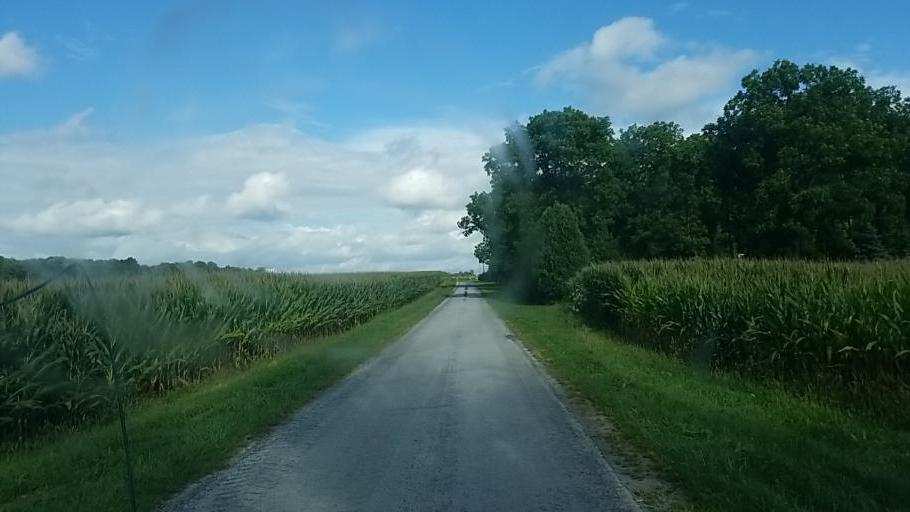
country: US
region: Ohio
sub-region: Hardin County
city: Kenton
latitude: 40.6800
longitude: -83.5433
